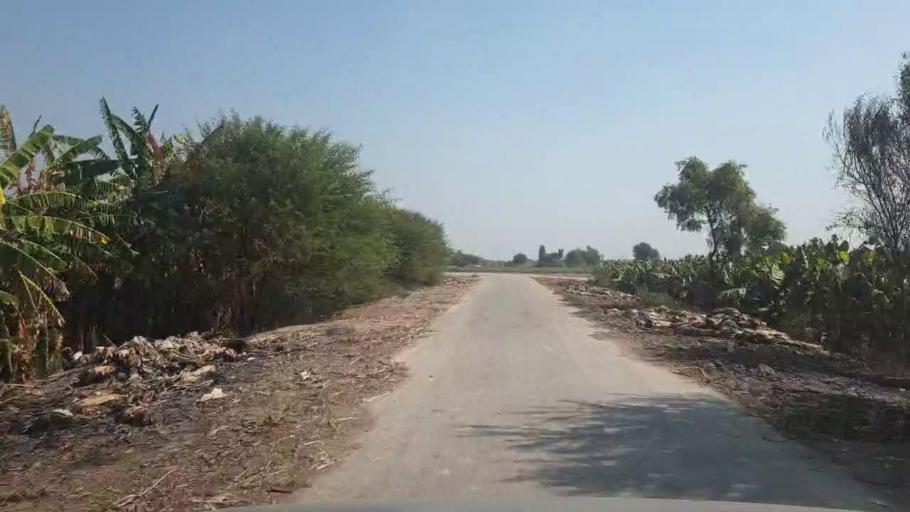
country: PK
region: Sindh
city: Chambar
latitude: 25.2416
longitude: 68.8581
